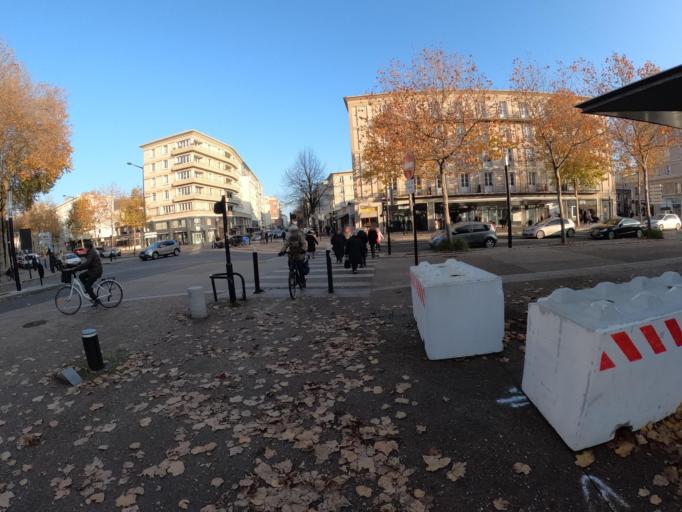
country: FR
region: Haute-Normandie
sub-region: Departement de la Seine-Maritime
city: Le Havre
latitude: 49.4945
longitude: 0.1091
